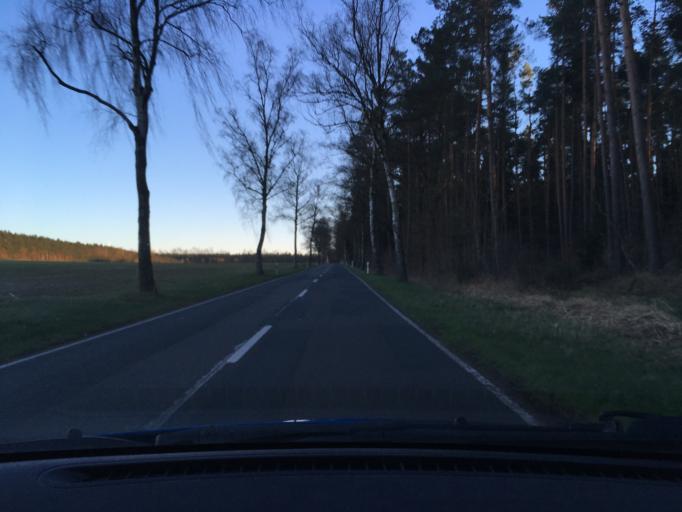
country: DE
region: Lower Saxony
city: Bleckede
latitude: 53.2500
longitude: 10.7464
